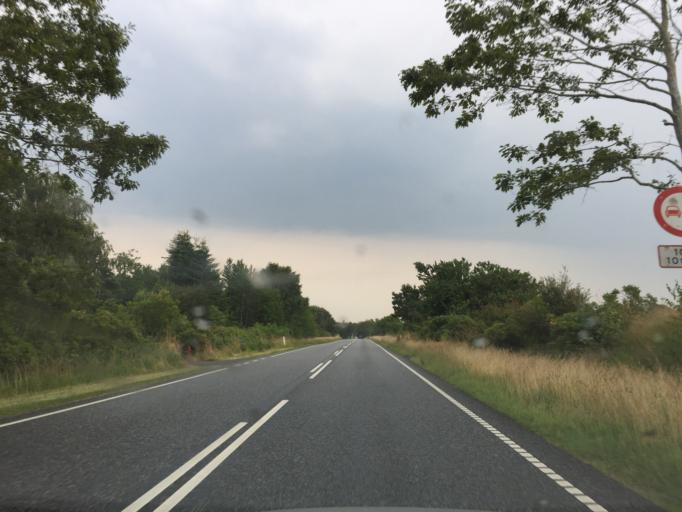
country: DK
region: Central Jutland
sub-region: Viborg Kommune
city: Bjerringbro
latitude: 56.3108
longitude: 9.5587
